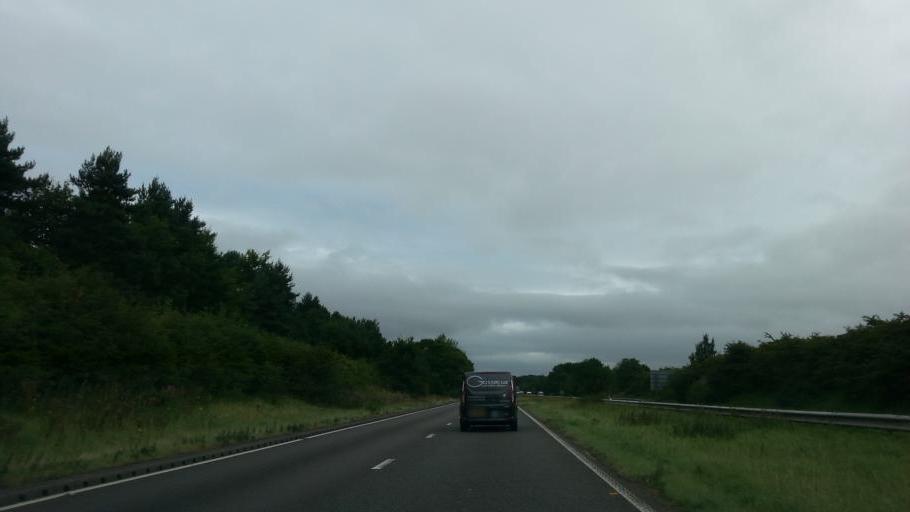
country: GB
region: England
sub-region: Nottinghamshire
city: Babworth
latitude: 53.3232
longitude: -1.0277
